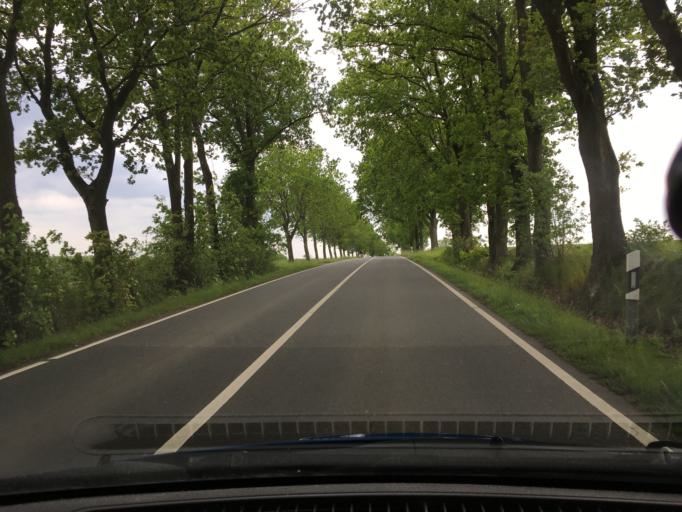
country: DE
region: Lower Saxony
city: Betzendorf
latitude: 53.1341
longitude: 10.3097
